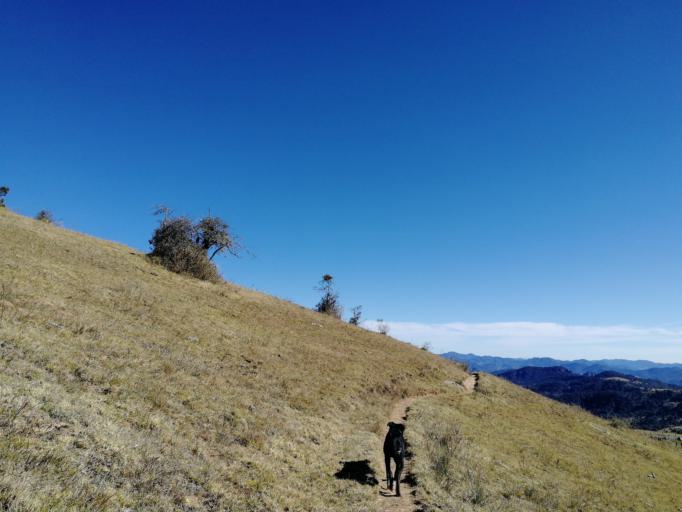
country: MX
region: San Luis Potosi
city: Zaragoza
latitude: 22.0052
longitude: -100.6132
